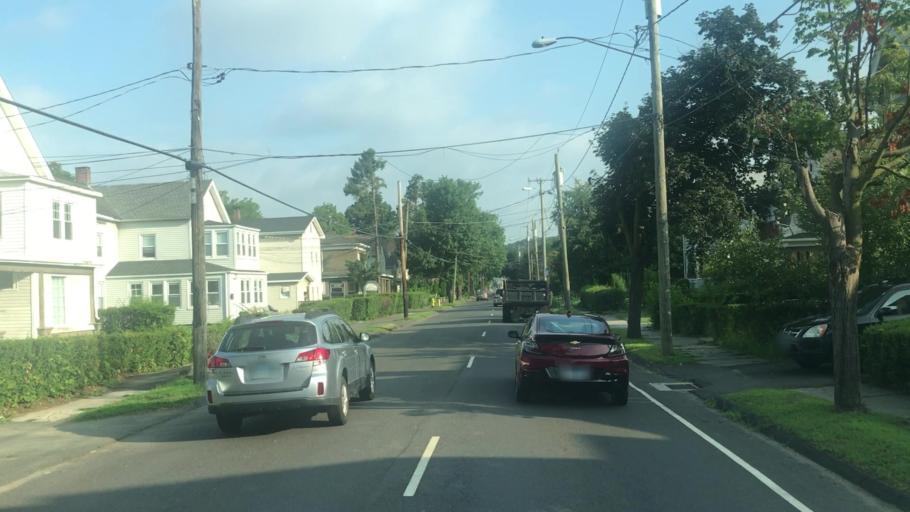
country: US
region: Connecticut
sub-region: Fairfield County
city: Danbury
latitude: 41.4006
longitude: -73.4532
